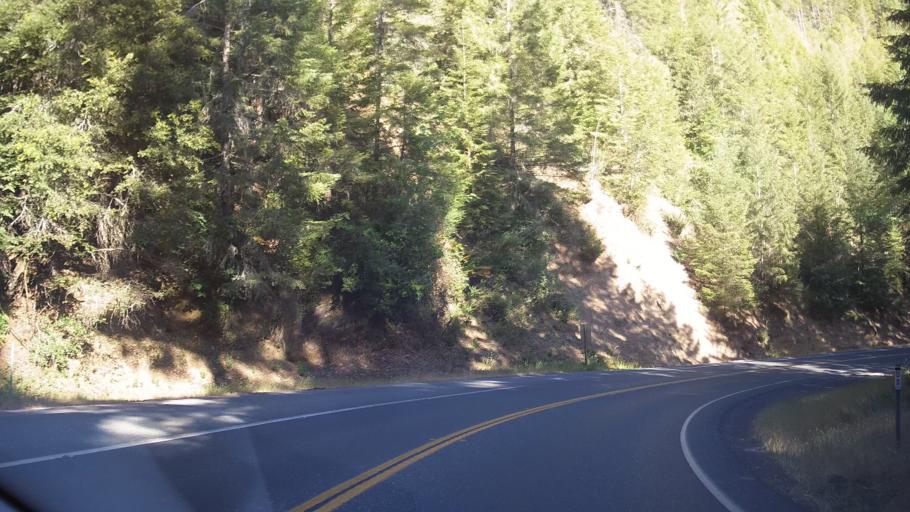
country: US
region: California
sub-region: Mendocino County
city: Brooktrails
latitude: 39.3535
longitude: -123.5095
